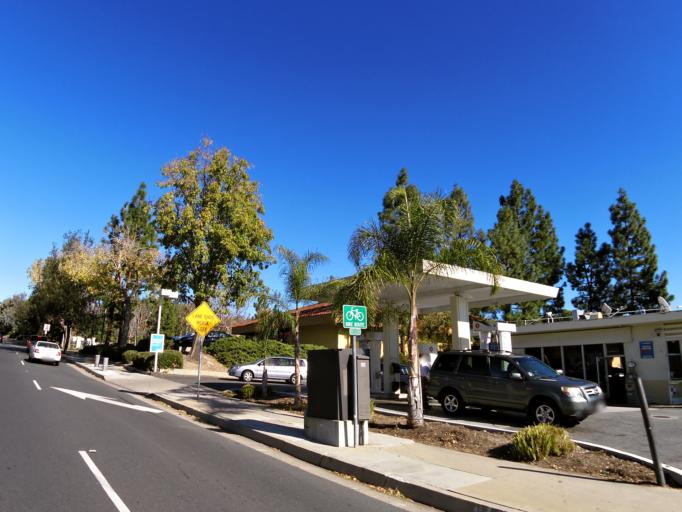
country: US
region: California
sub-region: Ventura County
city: Thousand Oaks
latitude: 34.1867
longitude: -118.8748
